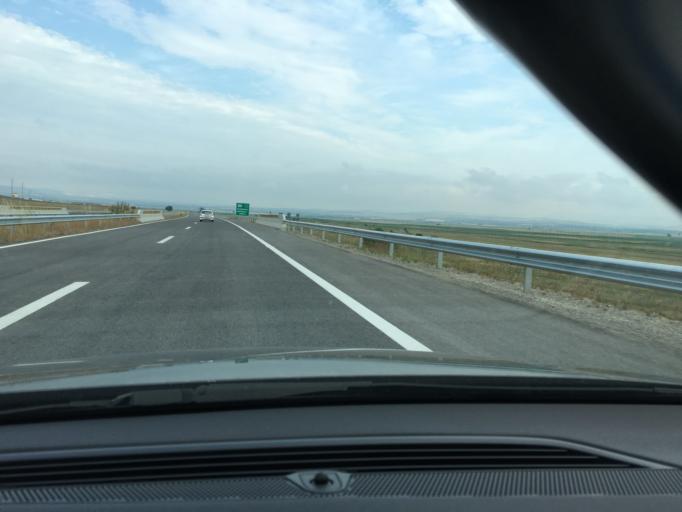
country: MK
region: Sveti Nikole
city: Sveti Nikole
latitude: 41.8050
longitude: 22.0693
